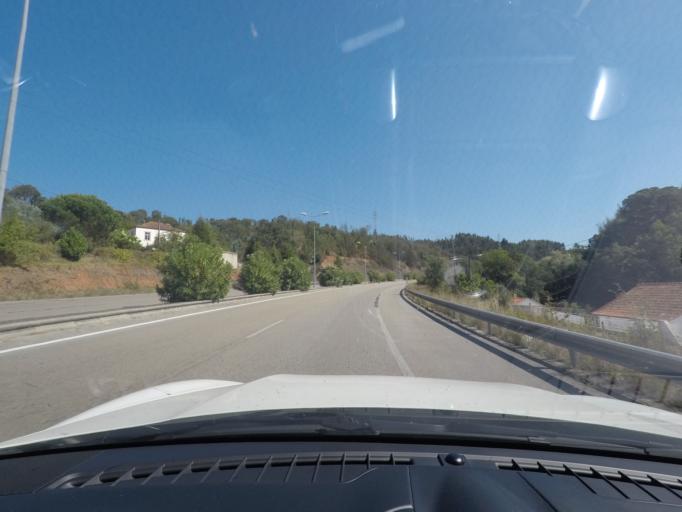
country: PT
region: Coimbra
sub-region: Coimbra
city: Coimbra
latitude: 40.2232
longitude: -8.3984
